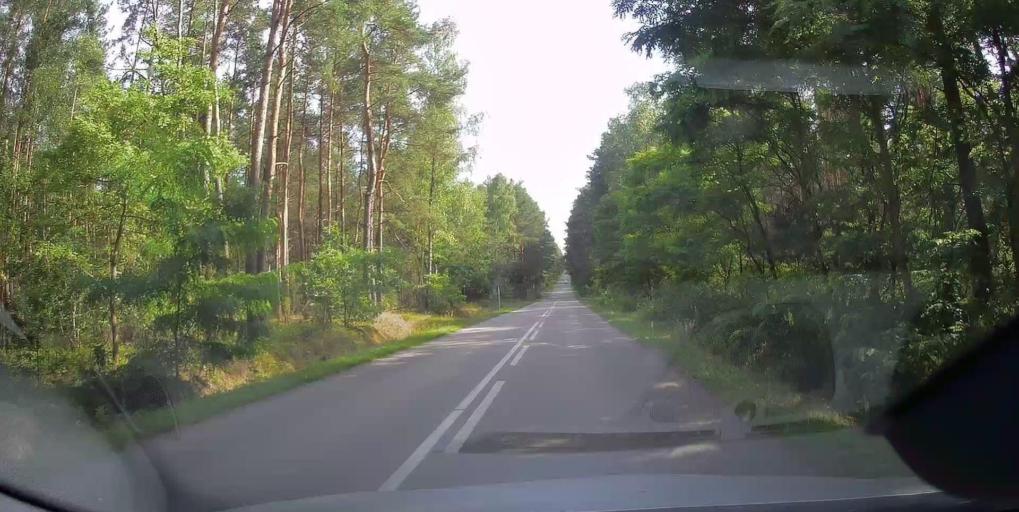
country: PL
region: Lodz Voivodeship
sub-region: Powiat opoczynski
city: Mniszkow
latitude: 51.3978
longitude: 20.0374
